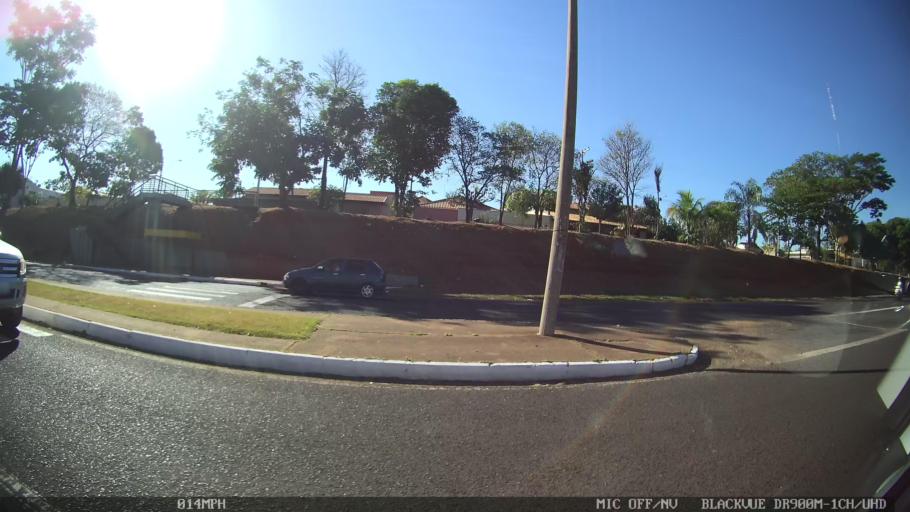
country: BR
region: Sao Paulo
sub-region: Olimpia
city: Olimpia
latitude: -20.7384
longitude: -48.8949
